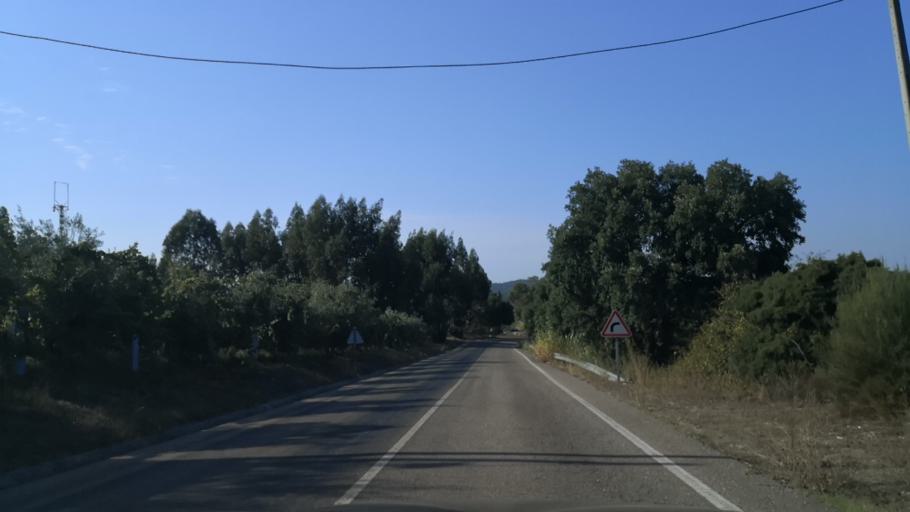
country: PT
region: Santarem
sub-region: Almeirim
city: Fazendas de Almeirim
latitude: 39.1002
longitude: -8.5769
